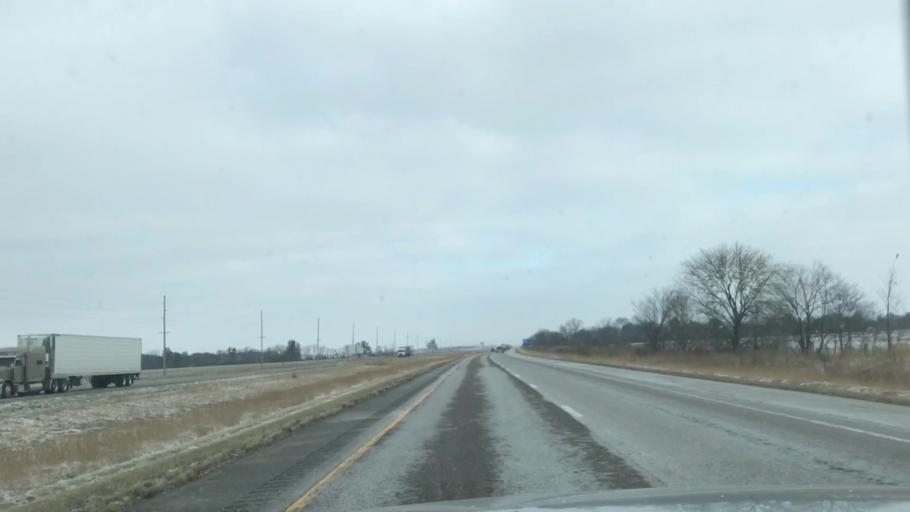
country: US
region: Illinois
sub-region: Macoupin County
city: Staunton
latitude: 38.9840
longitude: -89.7493
